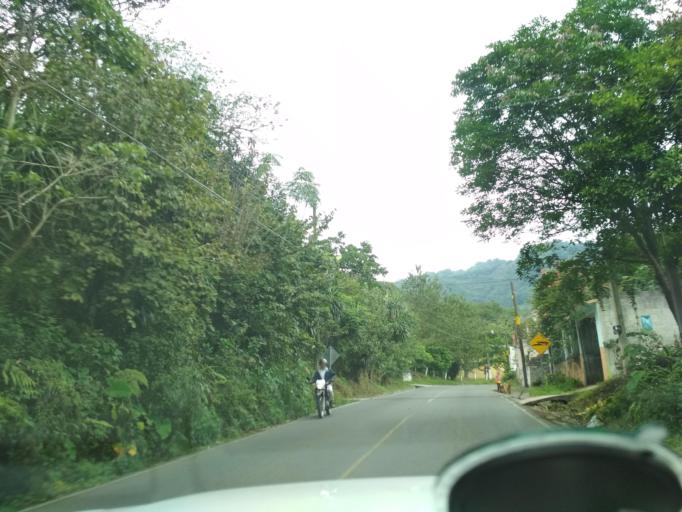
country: MX
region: Veracruz
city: Jilotepec
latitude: 19.6172
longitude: -96.9333
